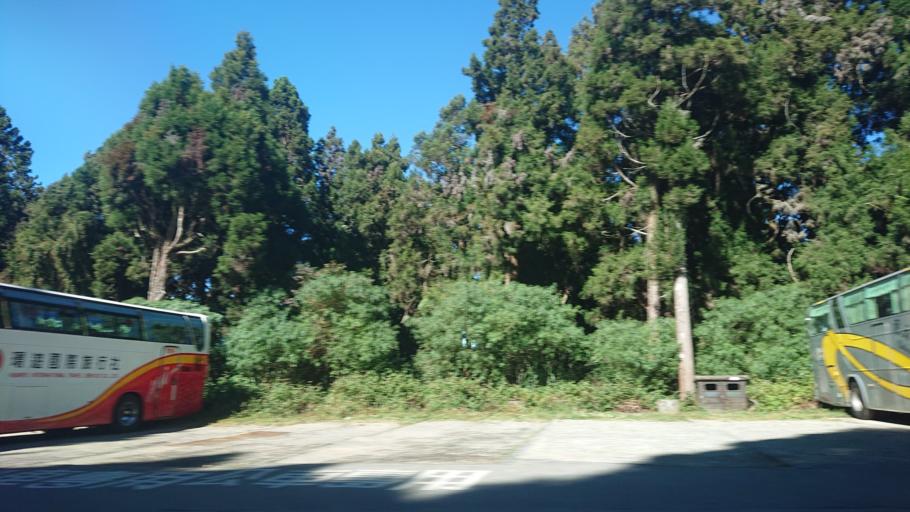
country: TW
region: Taiwan
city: Lugu
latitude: 23.5050
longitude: 120.7929
